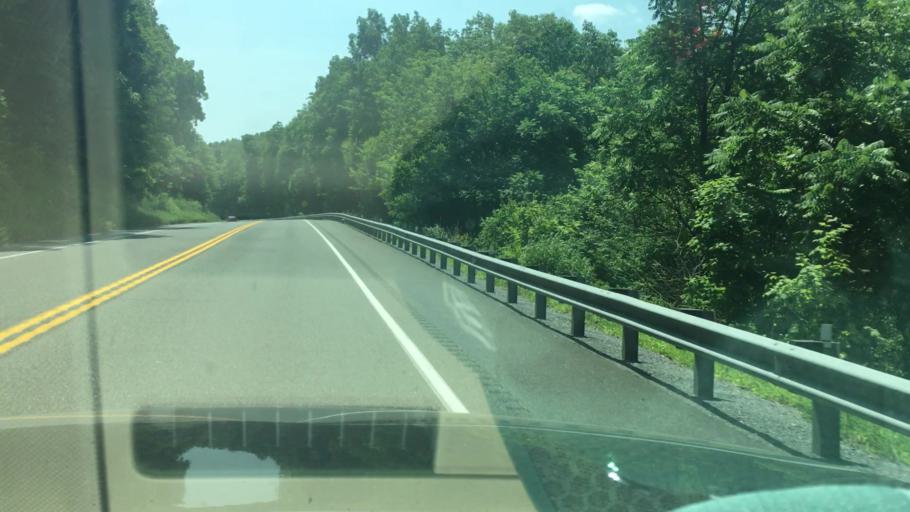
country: US
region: Pennsylvania
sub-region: Lehigh County
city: Schnecksville
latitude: 40.6620
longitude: -75.6870
